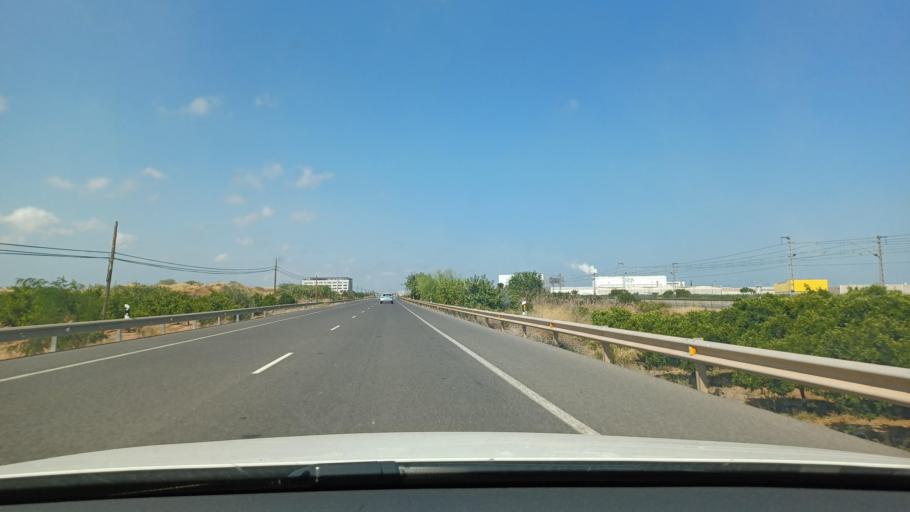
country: ES
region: Valencia
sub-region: Provincia de Castello
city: Chilches
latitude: 39.7895
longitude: -0.1854
